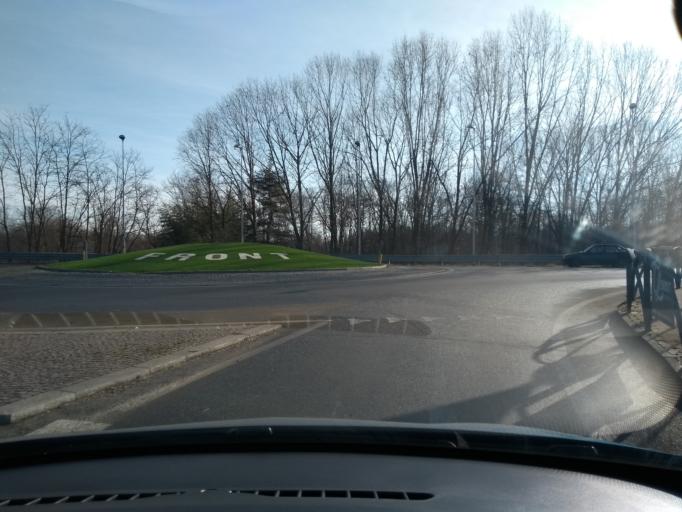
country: IT
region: Piedmont
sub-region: Provincia di Torino
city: Front
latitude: 45.2827
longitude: 7.6647
